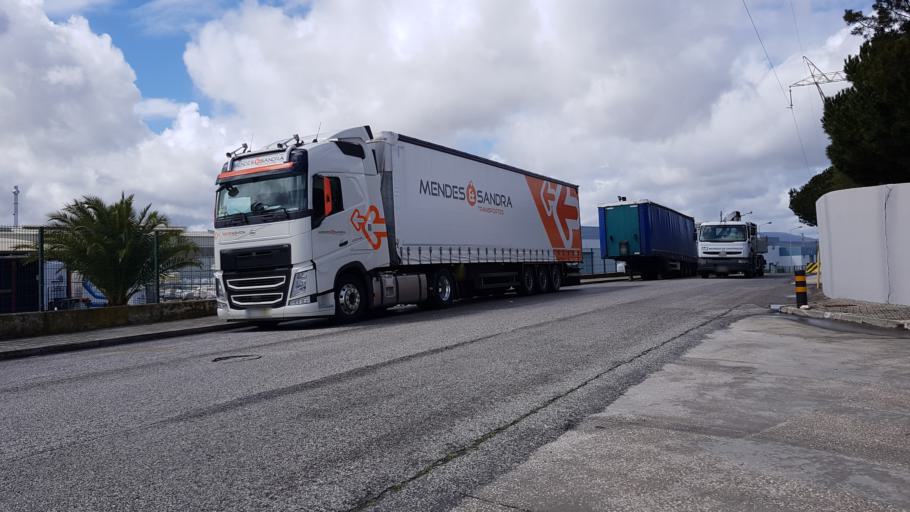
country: PT
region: Lisbon
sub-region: Alenquer
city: Carregado
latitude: 39.0351
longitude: -8.9708
